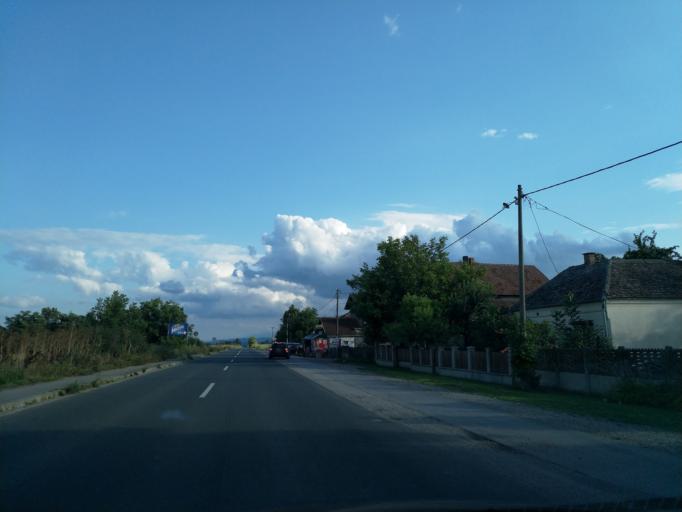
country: RS
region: Central Serbia
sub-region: Pomoravski Okrug
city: Paracin
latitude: 43.8024
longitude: 21.4218
